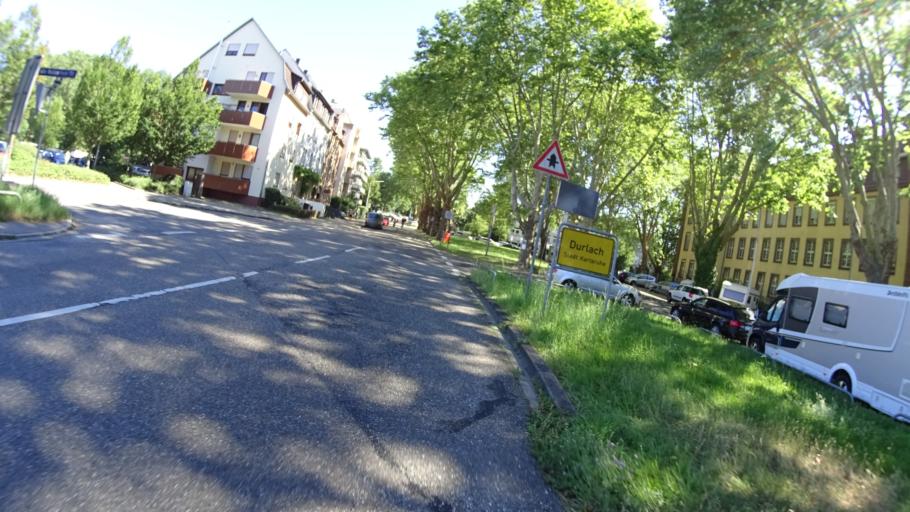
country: DE
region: Baden-Wuerttemberg
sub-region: Karlsruhe Region
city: Weingarten
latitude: 49.0051
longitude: 8.4780
